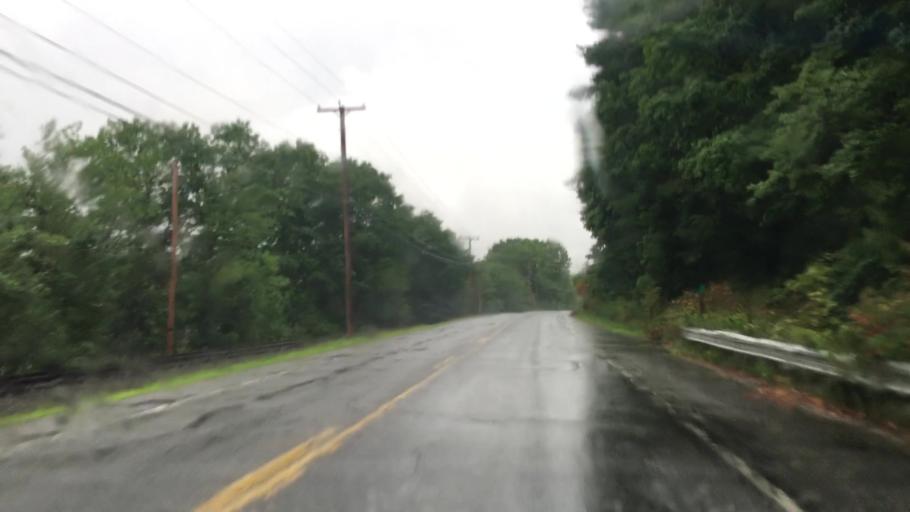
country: US
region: Maine
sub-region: Kennebec County
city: Pittston
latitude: 44.2155
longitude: -69.7625
